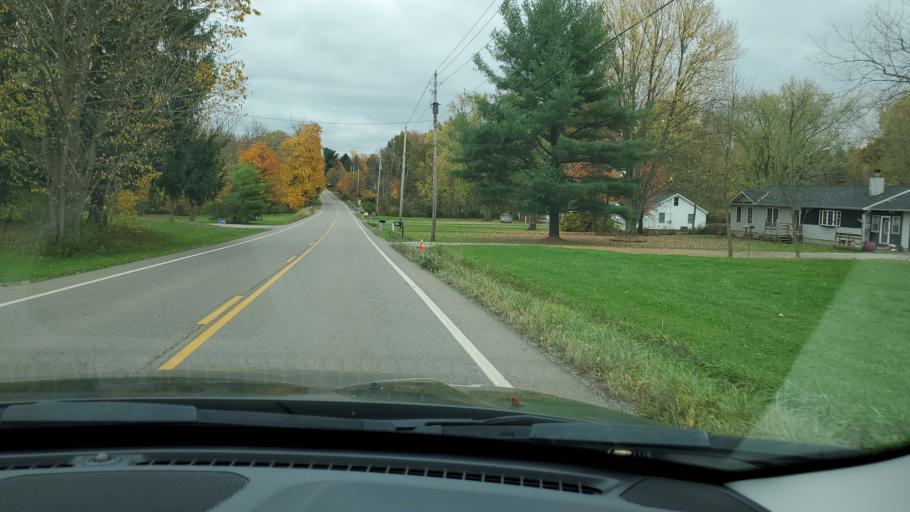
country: US
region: Ohio
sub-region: Mahoning County
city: Boardman
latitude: 40.9480
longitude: -80.6392
